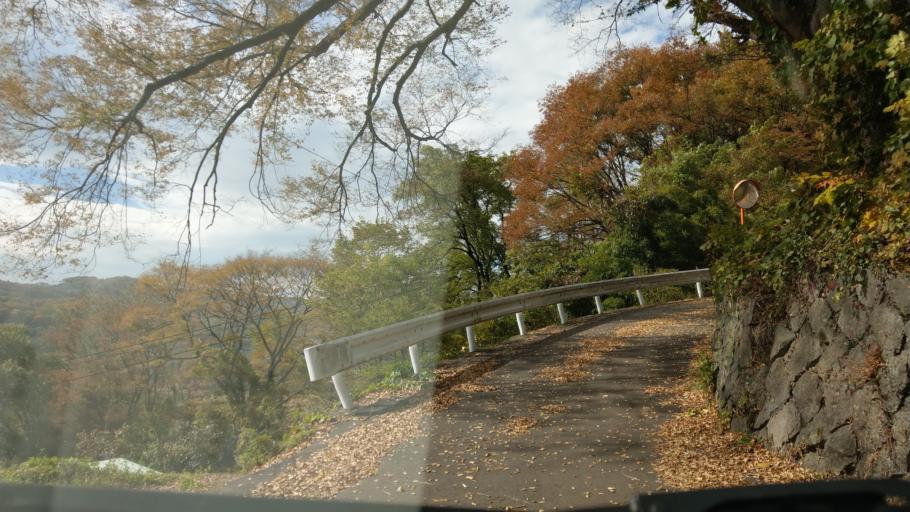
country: JP
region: Nagano
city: Komoro
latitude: 36.3302
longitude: 138.4128
